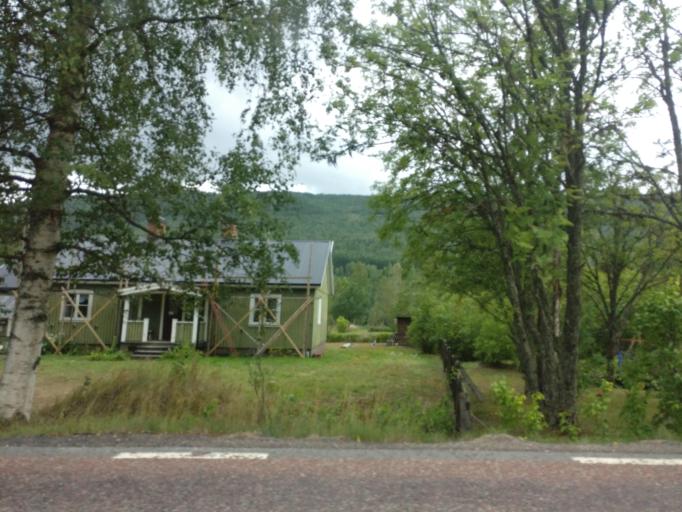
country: SE
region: Vaermland
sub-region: Torsby Kommun
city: Torsby
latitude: 60.7129
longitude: 12.8833
